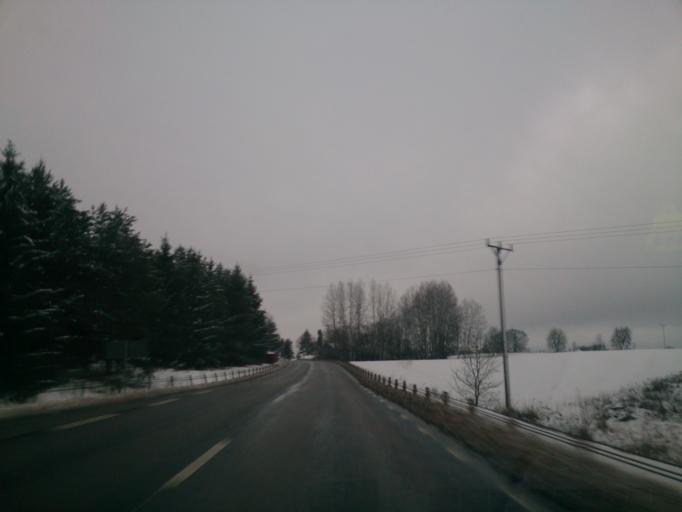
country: SE
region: OEstergoetland
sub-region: Linkopings Kommun
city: Sturefors
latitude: 58.3154
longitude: 15.8723
